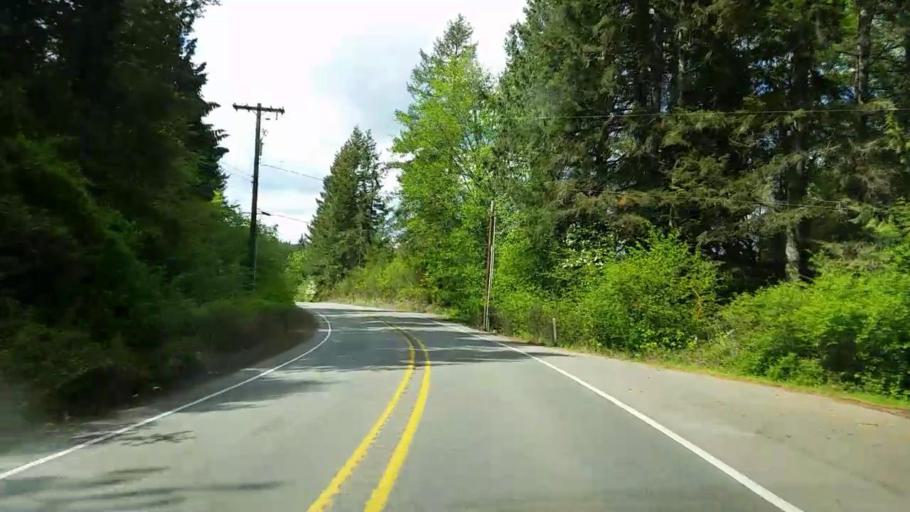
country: US
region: Washington
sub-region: Pierce County
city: Key Center
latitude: 47.3727
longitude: -122.7731
